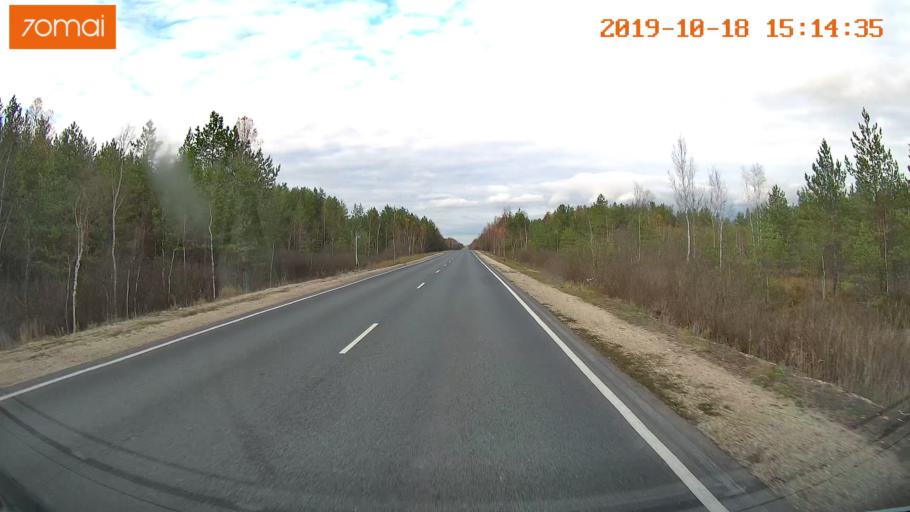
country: RU
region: Vladimir
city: Gus'-Khrustal'nyy
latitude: 55.6051
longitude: 40.7206
